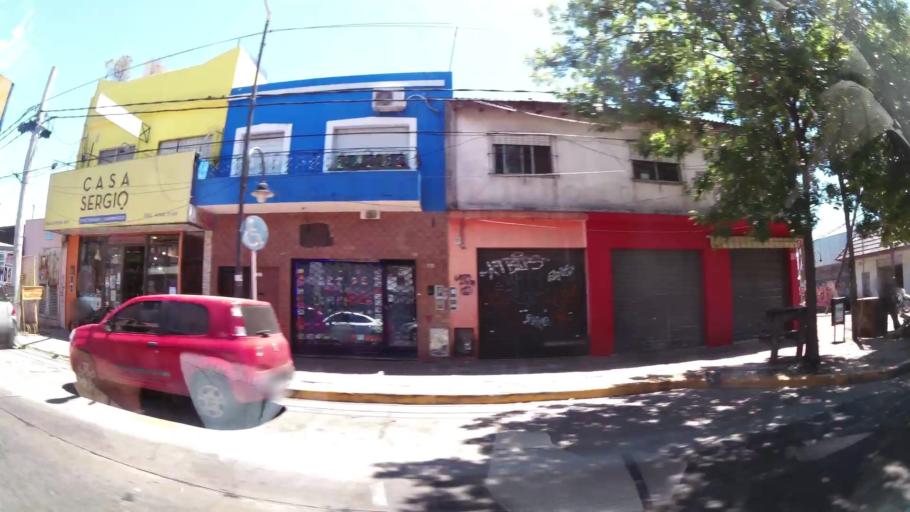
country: AR
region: Buenos Aires
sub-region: Partido de Tigre
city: Tigre
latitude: -34.4551
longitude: -58.5608
